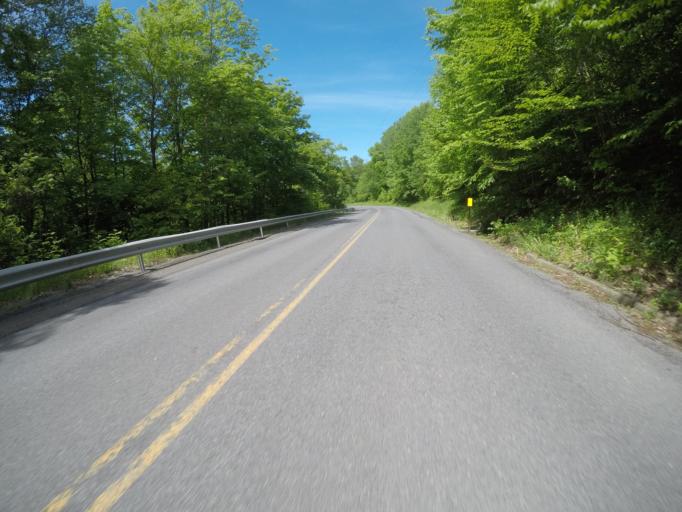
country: US
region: New York
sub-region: Delaware County
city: Delhi
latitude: 42.1155
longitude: -74.8203
